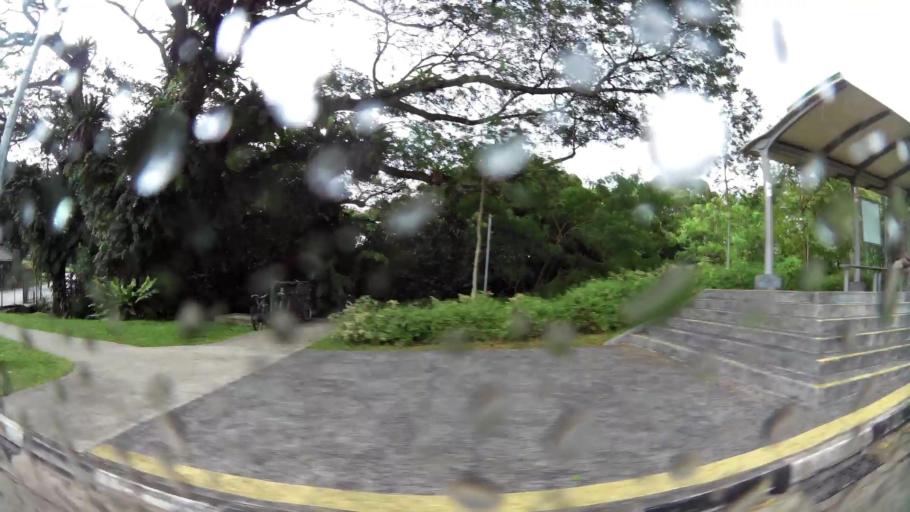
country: MY
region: Johor
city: Kampung Pasir Gudang Baru
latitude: 1.4022
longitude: 103.8720
